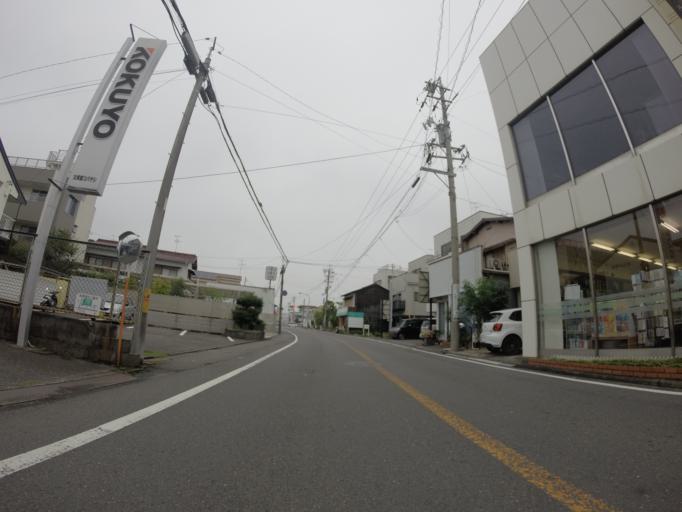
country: JP
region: Shizuoka
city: Shizuoka-shi
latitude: 34.9589
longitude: 138.3900
